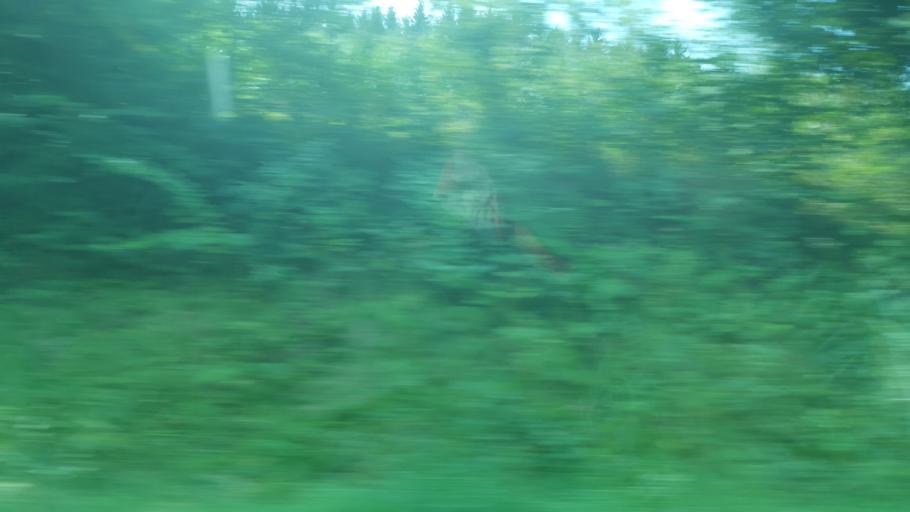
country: DE
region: Bavaria
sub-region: Upper Palatinate
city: Chamerau
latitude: 49.1859
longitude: 12.7373
